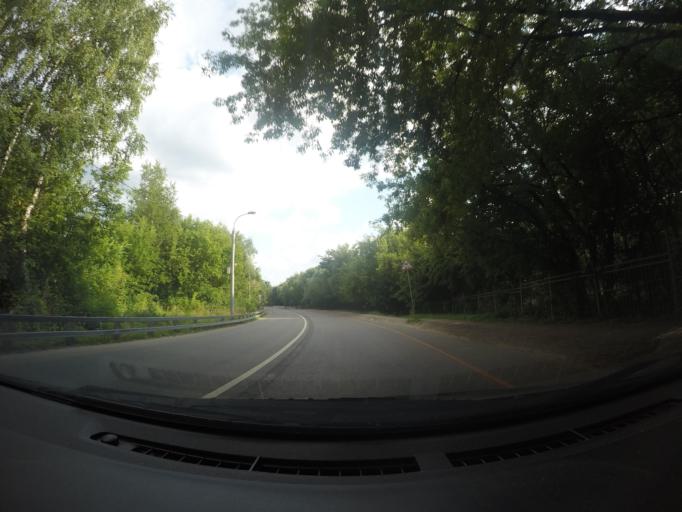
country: RU
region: Moscow
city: Sviblovo
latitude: 55.8450
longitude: 37.6267
